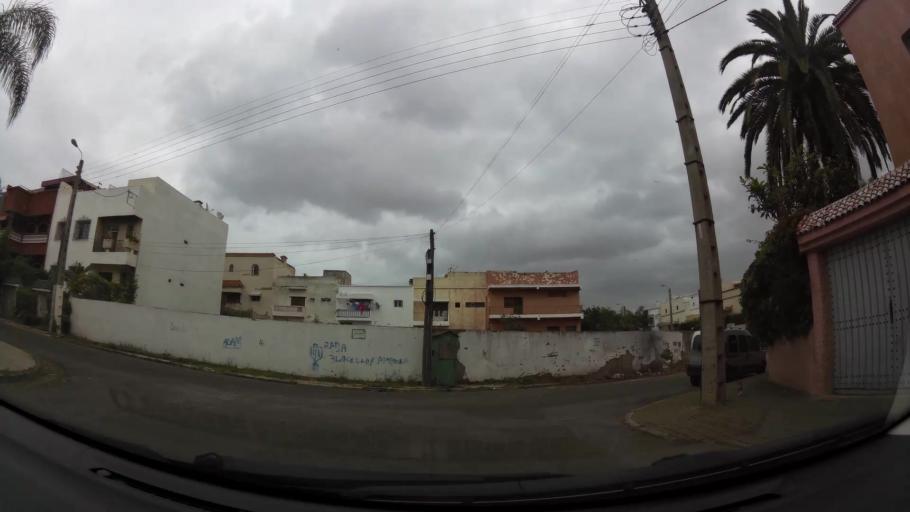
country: MA
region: Grand Casablanca
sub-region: Casablanca
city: Casablanca
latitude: 33.5742
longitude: -7.6697
